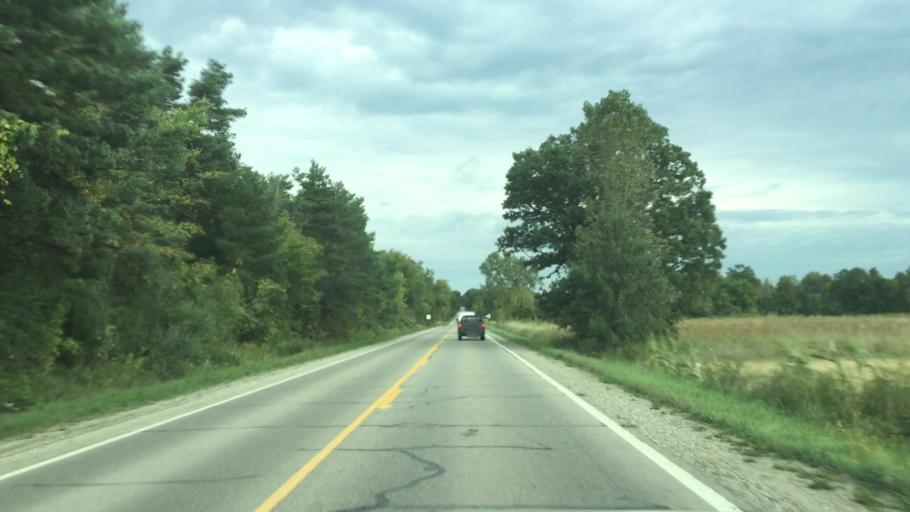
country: US
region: Michigan
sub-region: Livingston County
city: Howell
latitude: 42.6416
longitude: -83.8759
